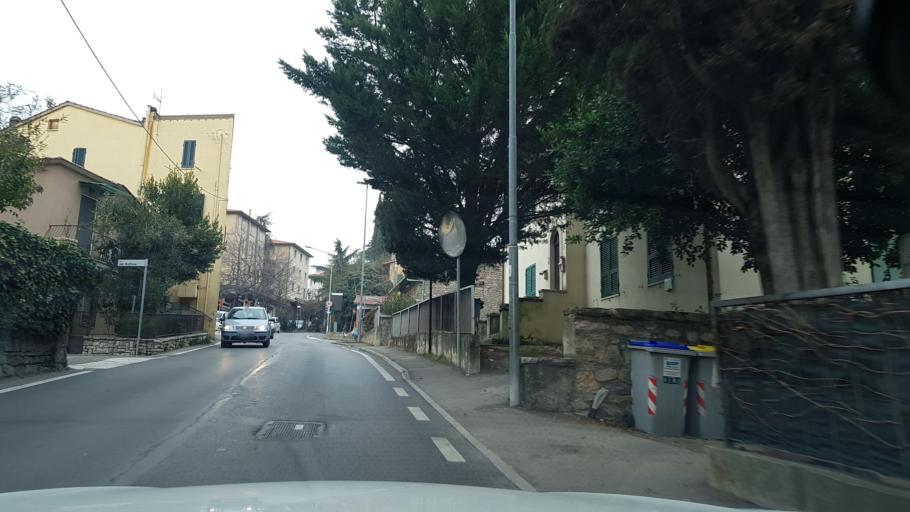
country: IT
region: Umbria
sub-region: Provincia di Perugia
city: Perugia
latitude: 43.1173
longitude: 12.3647
